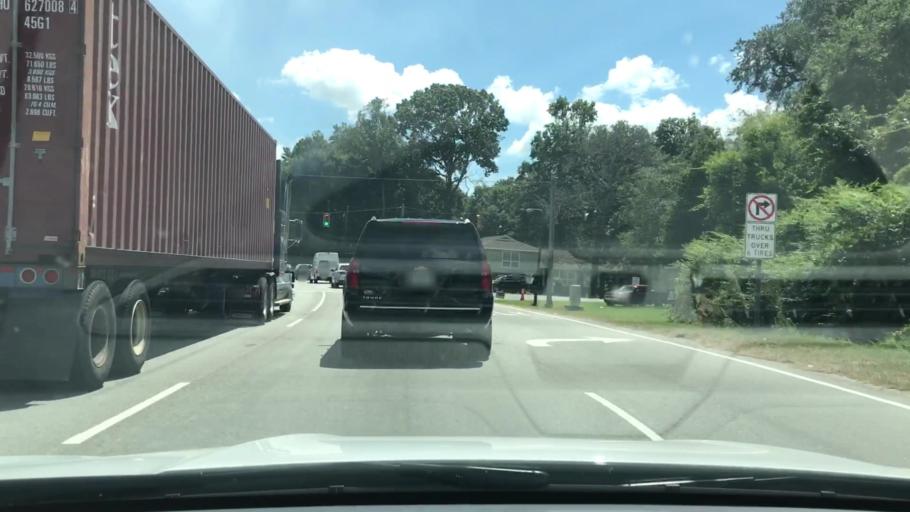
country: US
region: South Carolina
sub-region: Berkeley County
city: Hanahan
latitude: 32.9200
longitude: -79.9906
